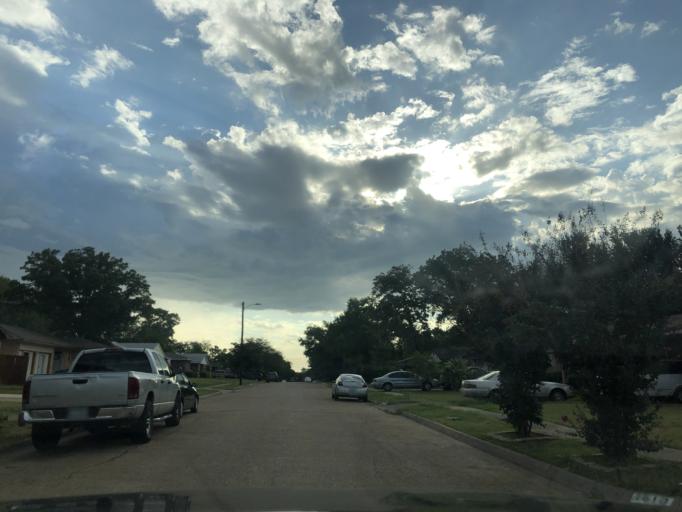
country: US
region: Texas
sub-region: Dallas County
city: Garland
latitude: 32.8762
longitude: -96.6520
